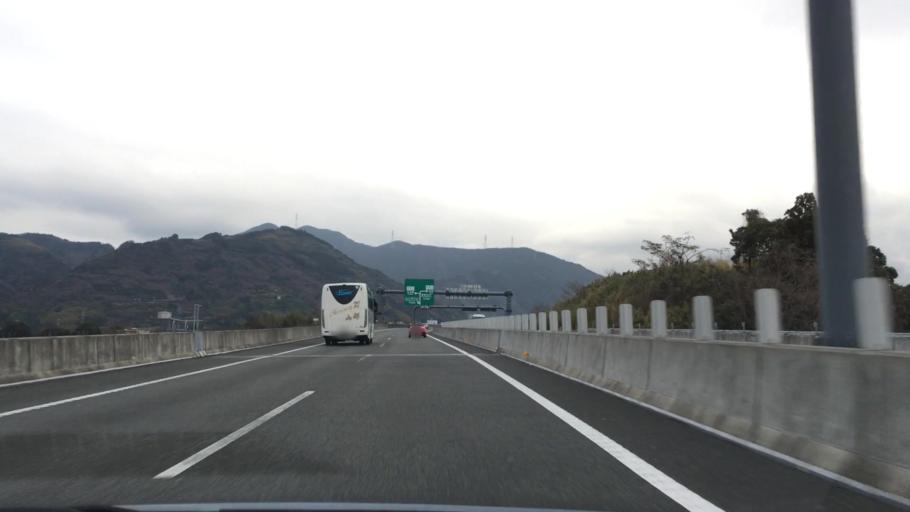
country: JP
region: Shizuoka
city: Shizuoka-shi
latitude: 35.0513
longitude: 138.4860
